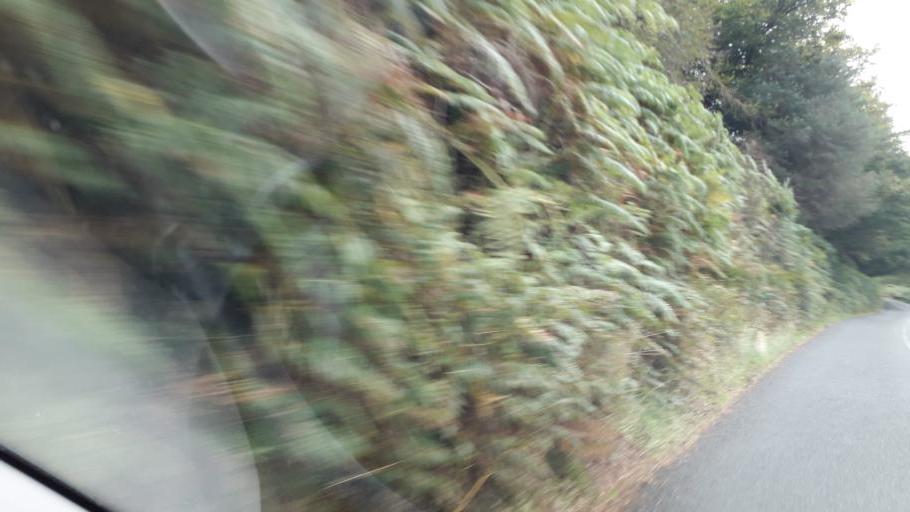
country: IE
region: Leinster
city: Ballyboden
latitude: 53.2404
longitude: -6.2893
